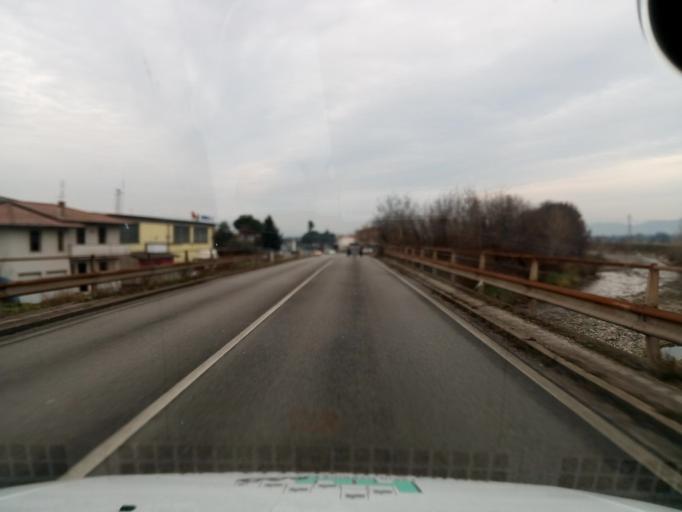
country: IT
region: Veneto
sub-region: Provincia di Vicenza
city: Montebello Vicentino
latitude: 45.4620
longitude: 11.3892
